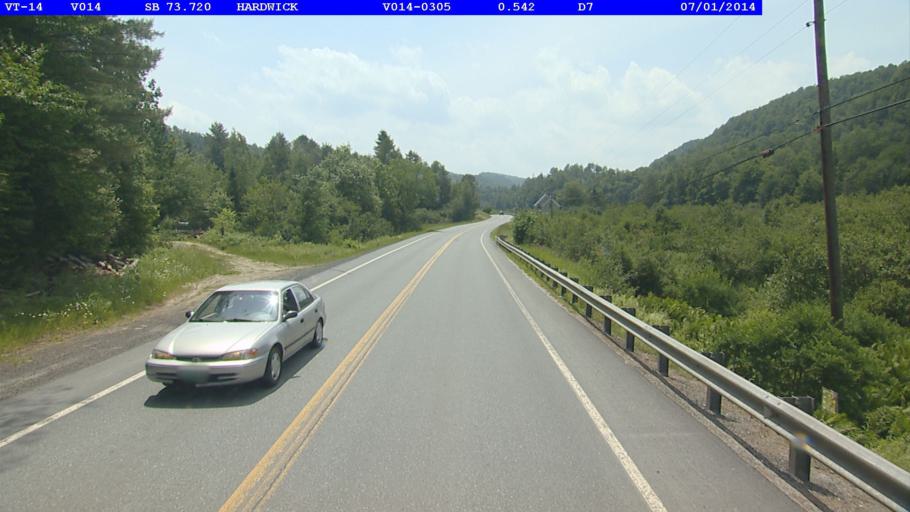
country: US
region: Vermont
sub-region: Caledonia County
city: Hardwick
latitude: 44.4927
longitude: -72.3768
